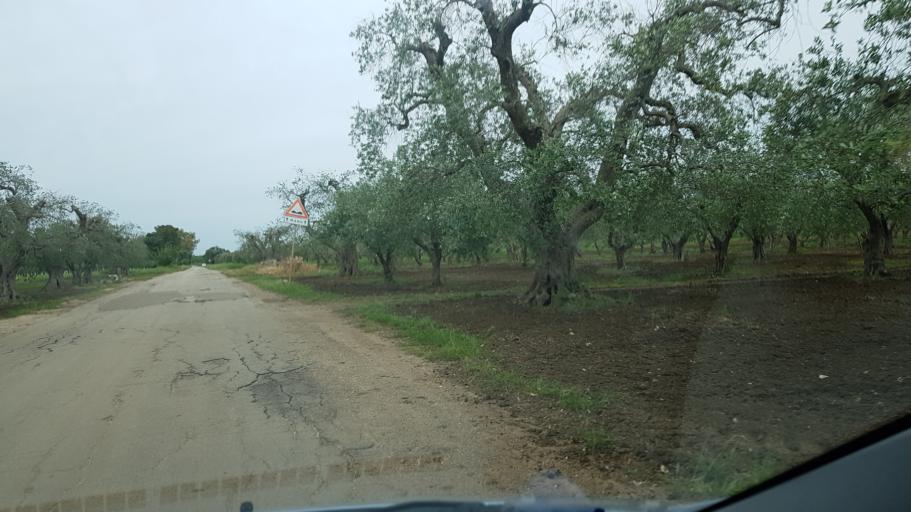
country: IT
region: Apulia
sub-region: Provincia di Brindisi
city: San Vito dei Normanni
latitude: 40.6208
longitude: 17.7698
